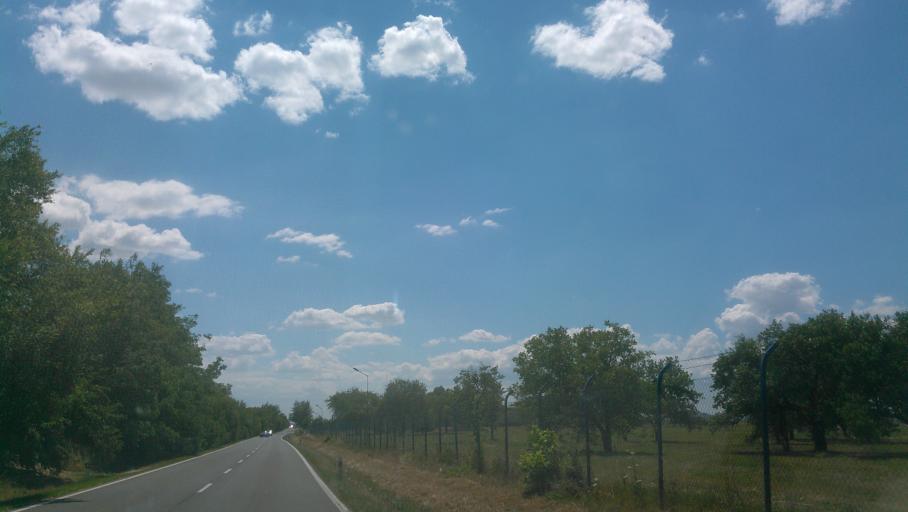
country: SK
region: Trnavsky
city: Leopoldov
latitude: 48.5205
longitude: 17.7288
